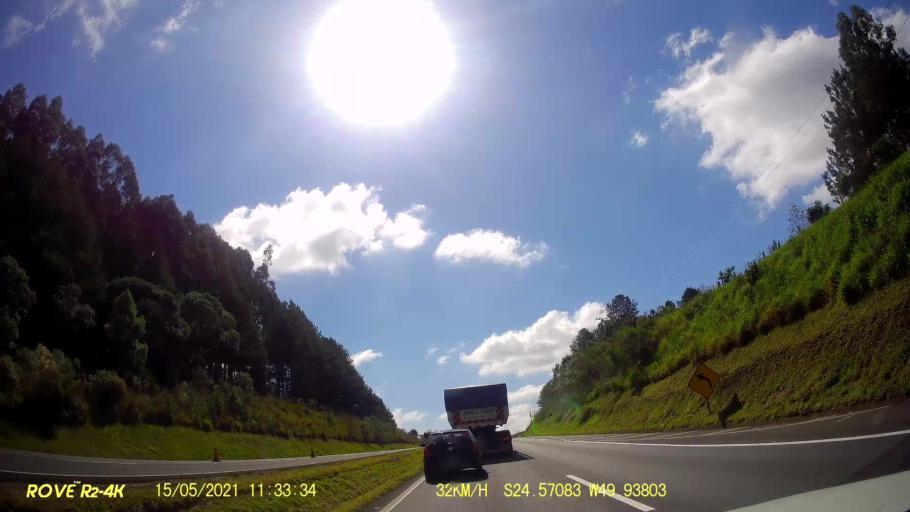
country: BR
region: Parana
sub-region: Pirai Do Sul
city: Pirai do Sul
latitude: -24.5709
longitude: -49.9381
